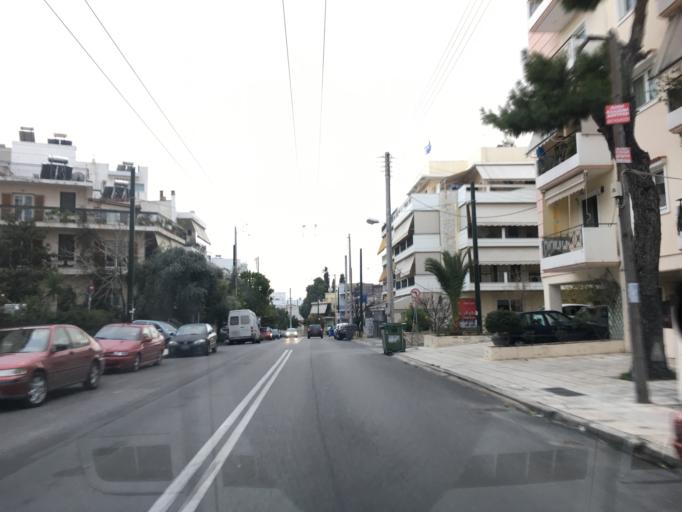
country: GR
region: Attica
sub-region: Nomarchia Athinas
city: Nea Filadelfeia
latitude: 38.0492
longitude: 23.7391
